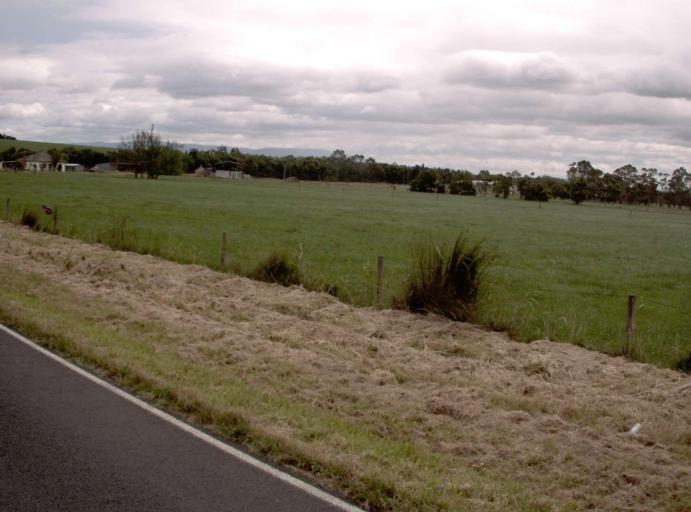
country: AU
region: Victoria
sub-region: Latrobe
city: Moe
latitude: -38.1756
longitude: 146.1456
